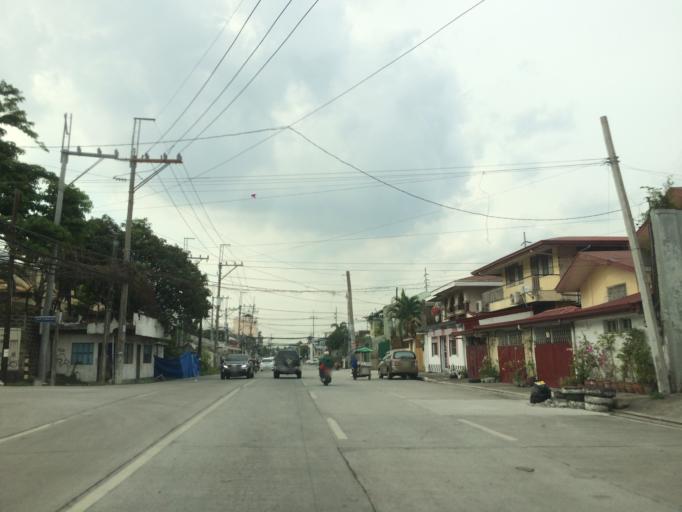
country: PH
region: Calabarzon
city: Del Monte
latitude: 14.6373
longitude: 121.0057
